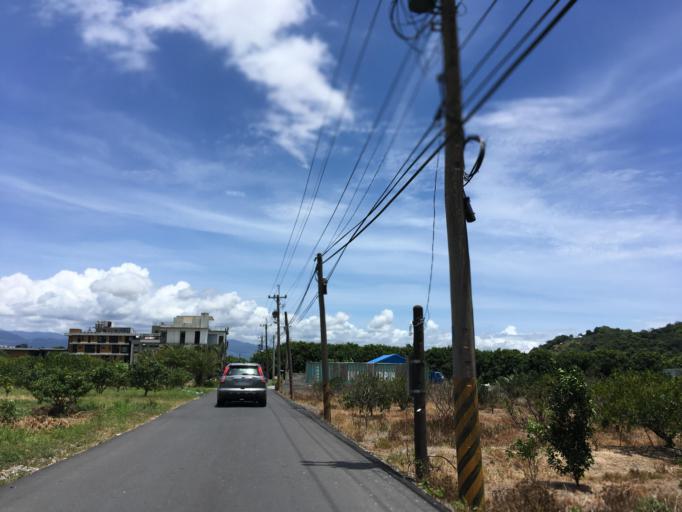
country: TW
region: Taiwan
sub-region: Yilan
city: Yilan
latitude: 24.6368
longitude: 121.7206
